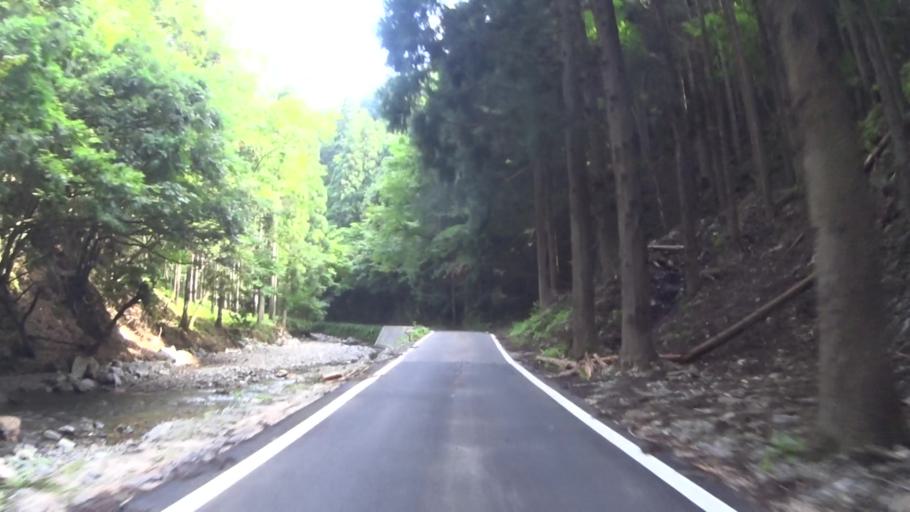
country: JP
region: Fukui
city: Obama
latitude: 35.2907
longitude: 135.6438
